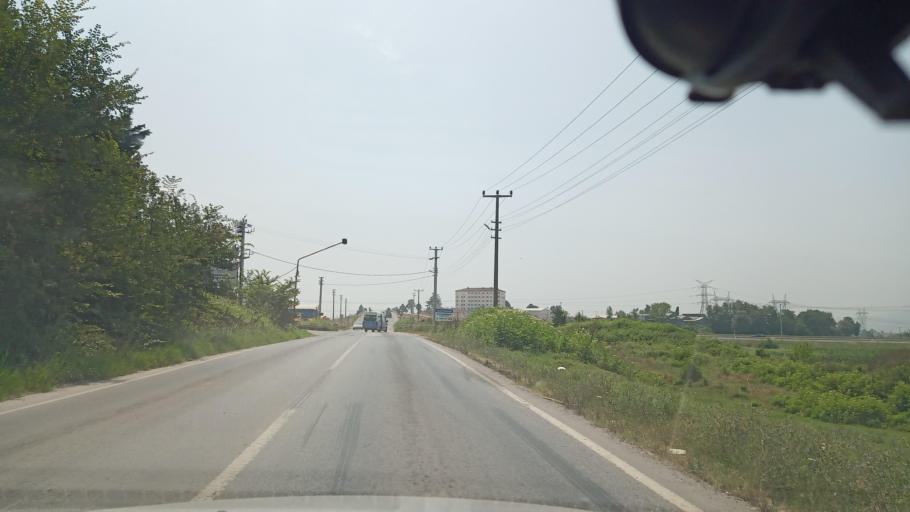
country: TR
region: Sakarya
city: Adapazari
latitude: 40.8279
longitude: 30.3965
